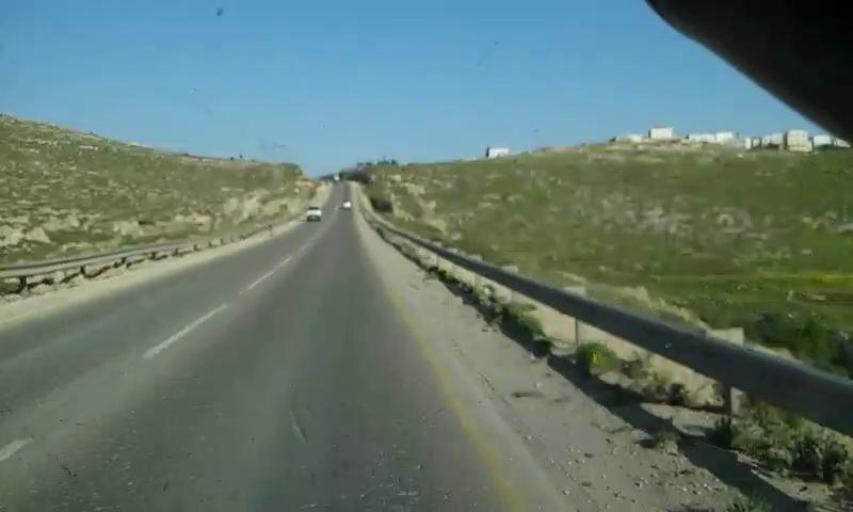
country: PS
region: West Bank
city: Qalqas
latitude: 31.4966
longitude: 35.0897
